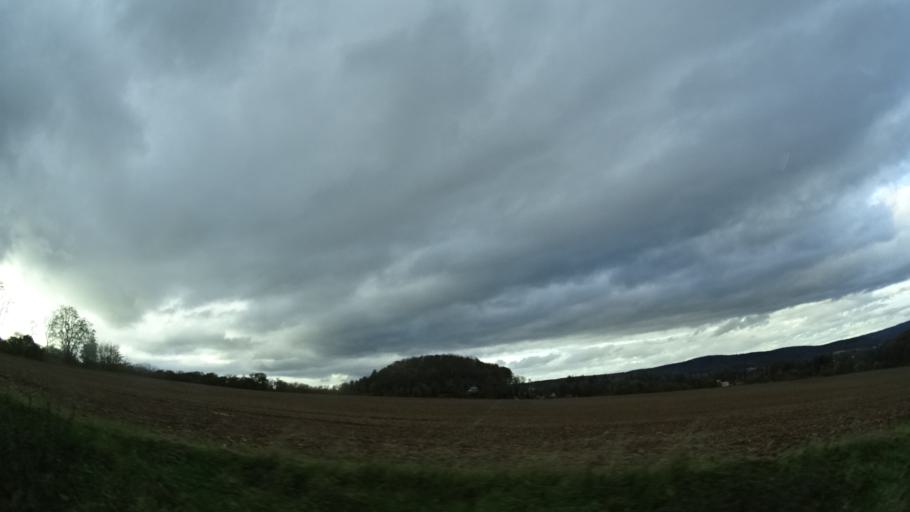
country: DE
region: Thuringia
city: Wernburg
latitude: 50.6824
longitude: 11.6063
